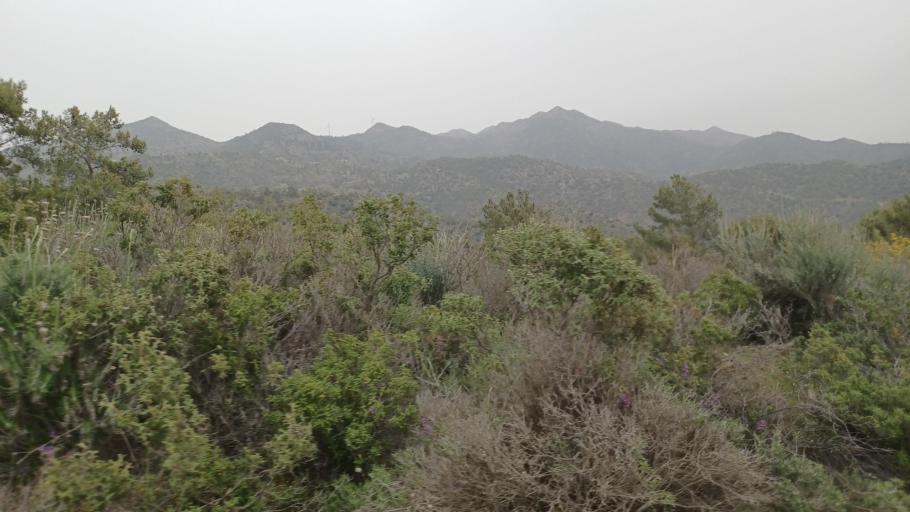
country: CY
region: Limassol
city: Pelendri
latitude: 34.8634
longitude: 33.0956
